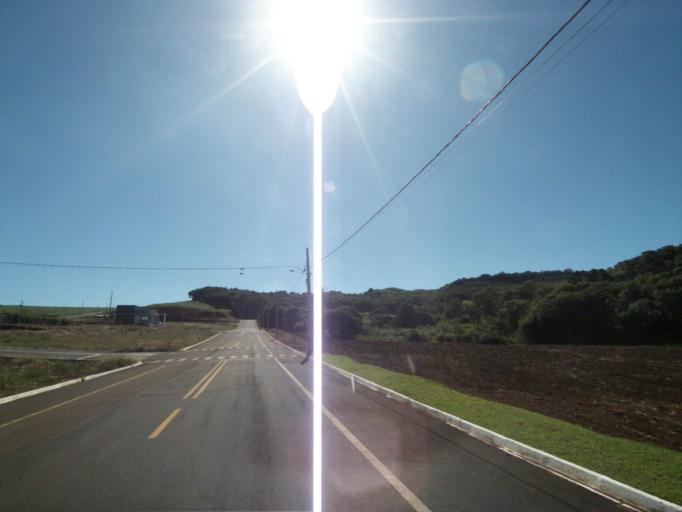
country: BR
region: Parana
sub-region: Pato Branco
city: Pato Branco
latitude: -26.2641
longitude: -52.7752
